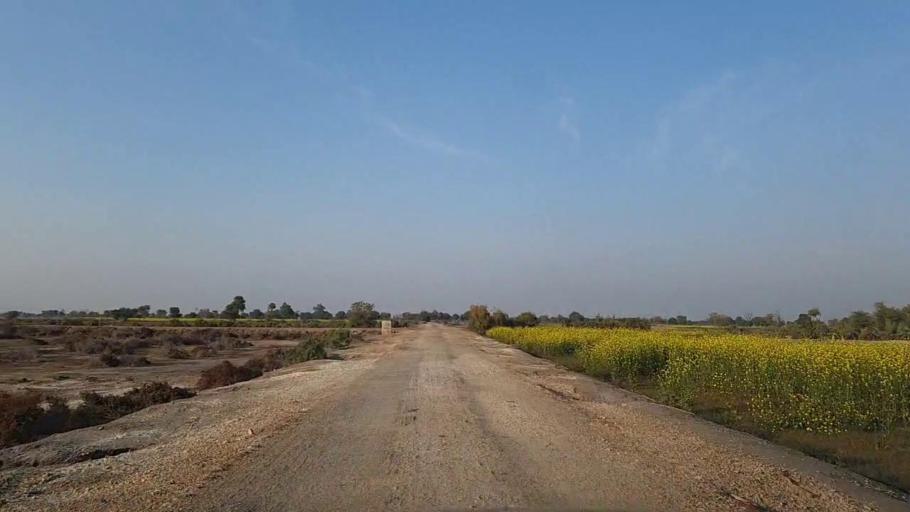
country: PK
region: Sindh
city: Jam Sahib
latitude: 26.3828
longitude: 68.5390
